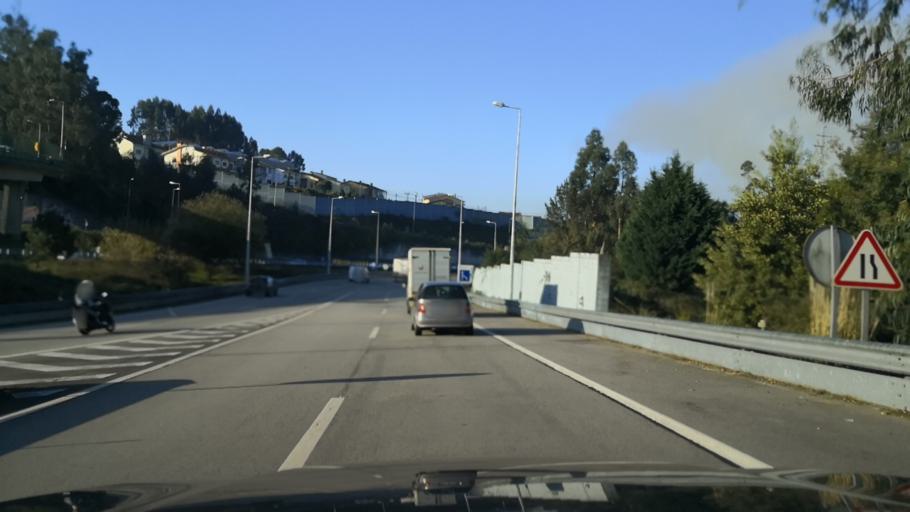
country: PT
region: Porto
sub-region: Maia
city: Pedroucos
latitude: 41.1981
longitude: -8.5911
